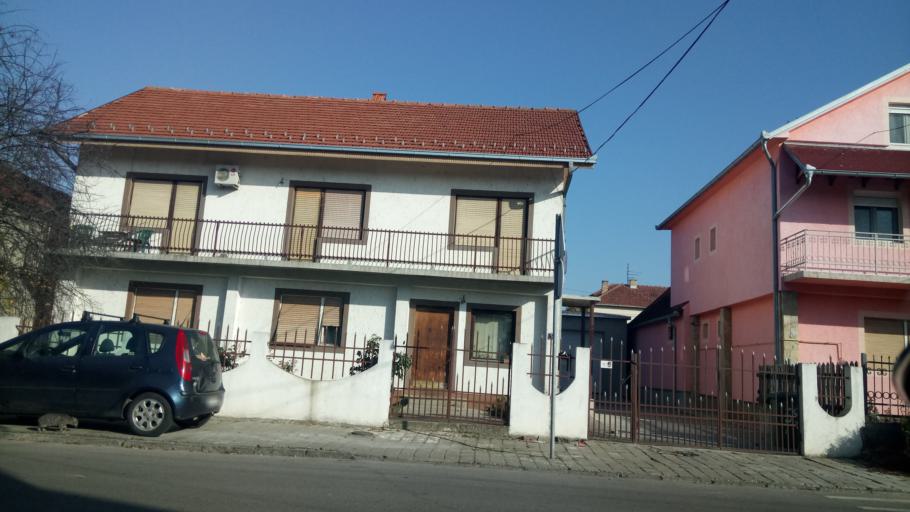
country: RS
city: Novi Banovci
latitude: 44.9013
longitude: 20.2896
